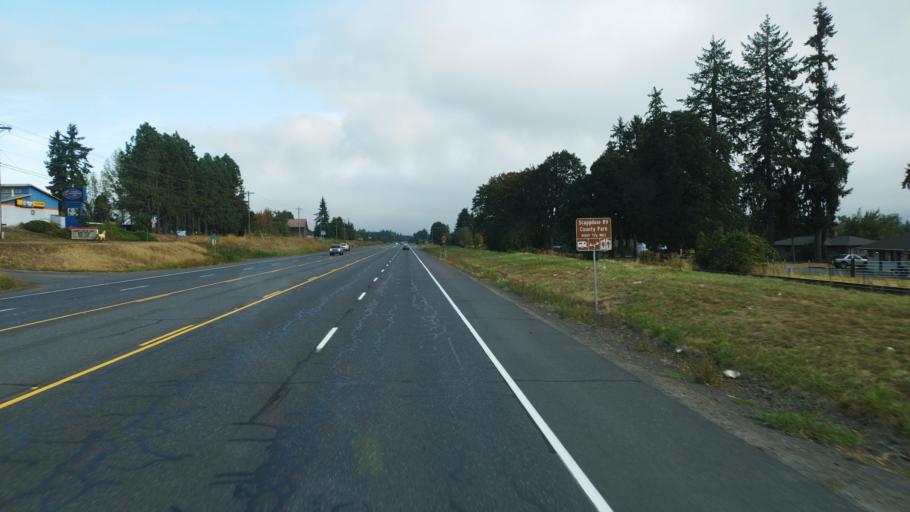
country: US
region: Oregon
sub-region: Columbia County
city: Scappoose
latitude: 45.7764
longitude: -122.8770
